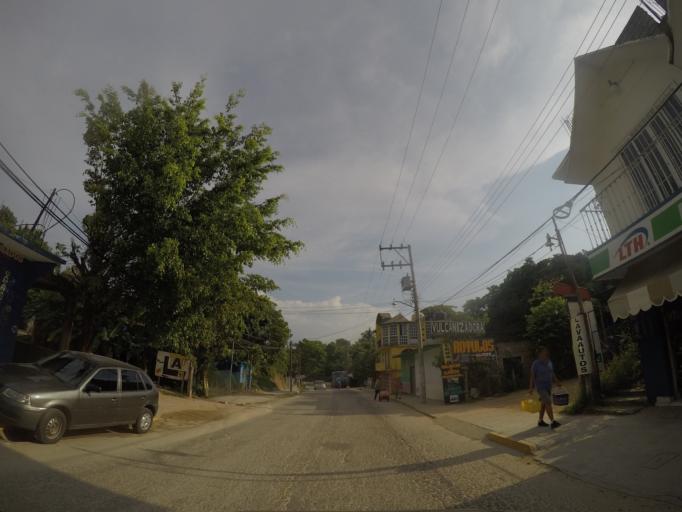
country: MX
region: Oaxaca
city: San Pedro Pochutla
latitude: 15.7517
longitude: -96.4645
